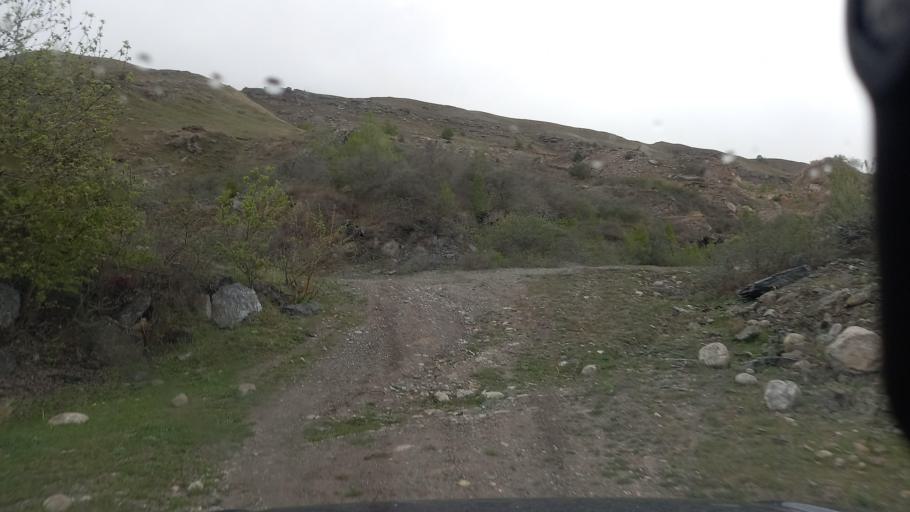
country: RU
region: Kabardino-Balkariya
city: Bylym
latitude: 43.4571
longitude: 42.9979
